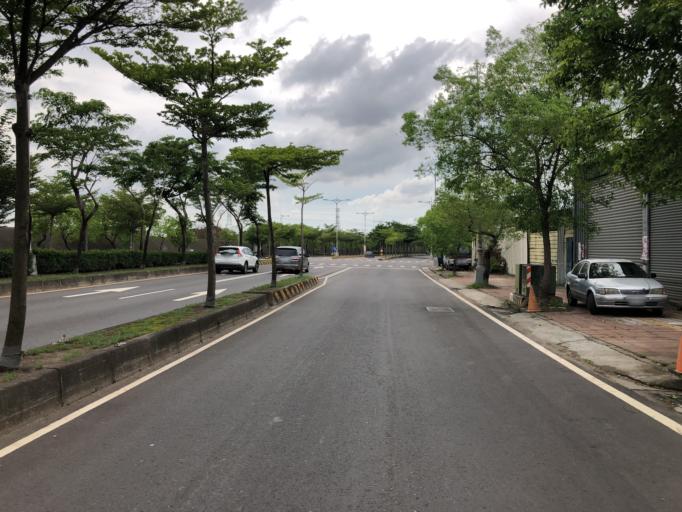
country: TW
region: Taiwan
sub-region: Taichung City
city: Taichung
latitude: 24.0947
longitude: 120.6337
